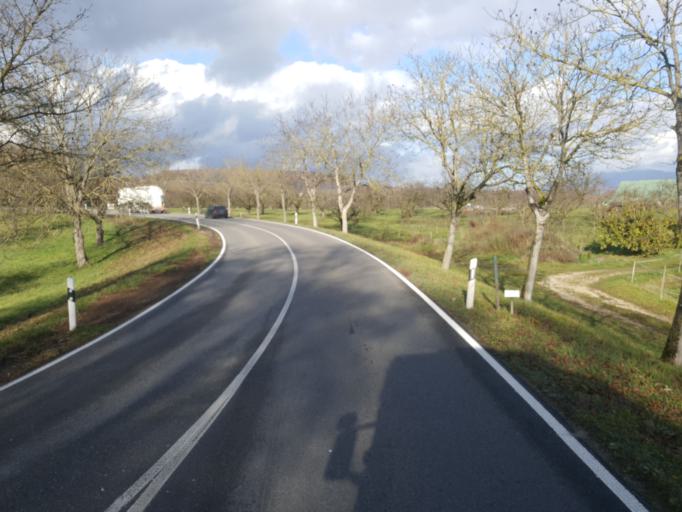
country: DE
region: Baden-Wuerttemberg
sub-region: Freiburg Region
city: Efringen-Kirchen
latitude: 47.6524
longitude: 7.5816
